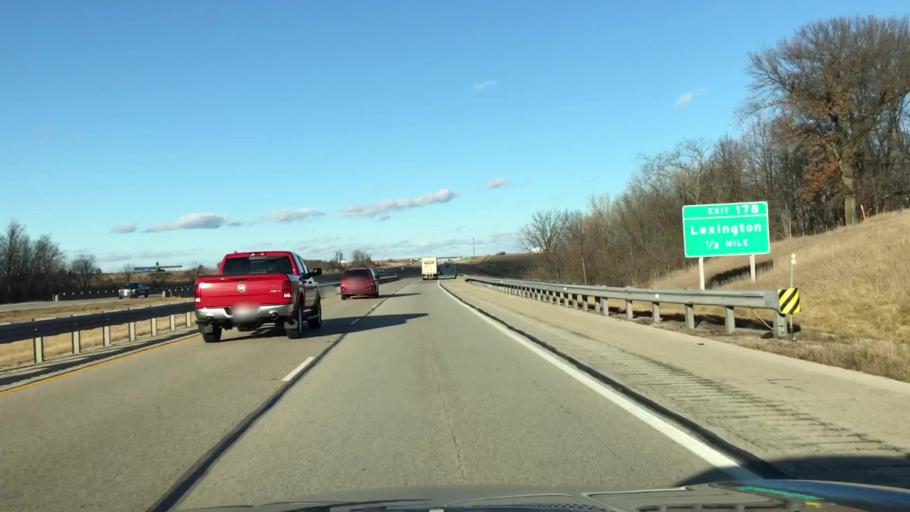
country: US
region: Illinois
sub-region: McLean County
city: Lexington
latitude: 40.6343
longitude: -88.8145
